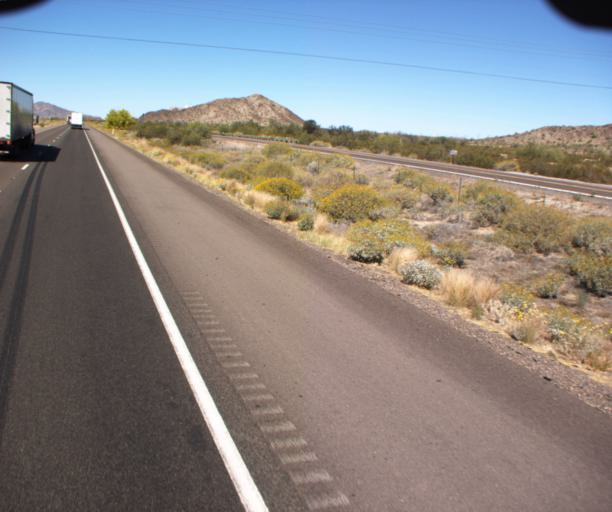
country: US
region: Arizona
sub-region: Maricopa County
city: Buckeye
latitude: 33.1741
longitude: -112.6504
